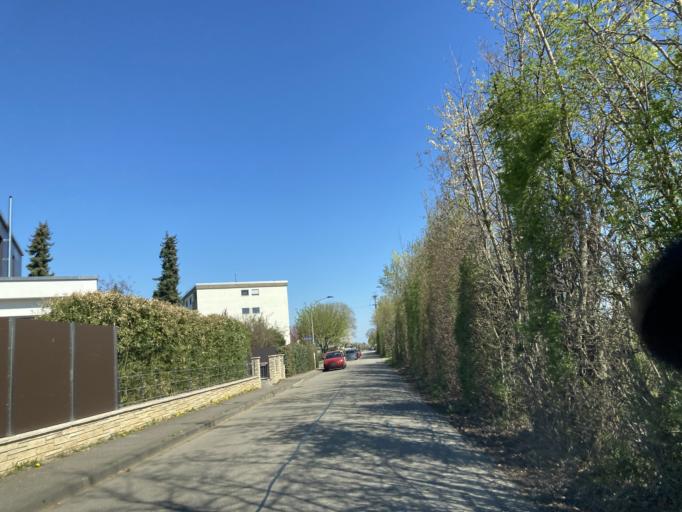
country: DE
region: Baden-Wuerttemberg
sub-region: Freiburg Region
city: Schliengen
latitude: 47.7704
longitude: 7.5576
